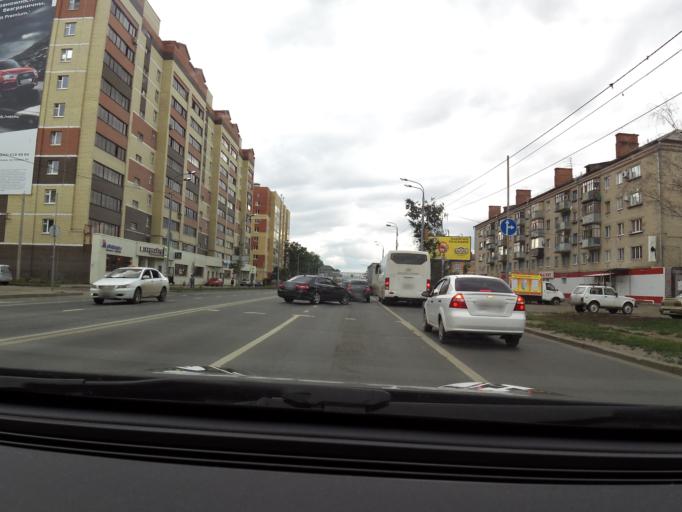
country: RU
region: Tatarstan
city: Staroye Arakchino
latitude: 55.8253
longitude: 49.0391
